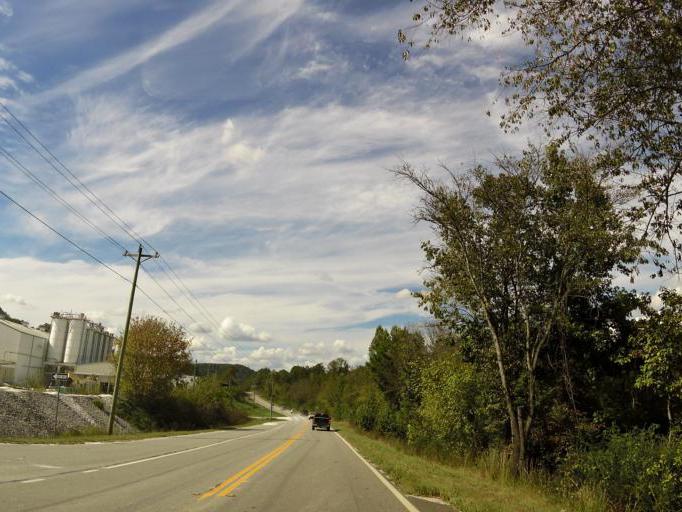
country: US
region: Georgia
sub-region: Pickens County
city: Nelson
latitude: 34.4214
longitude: -84.3243
